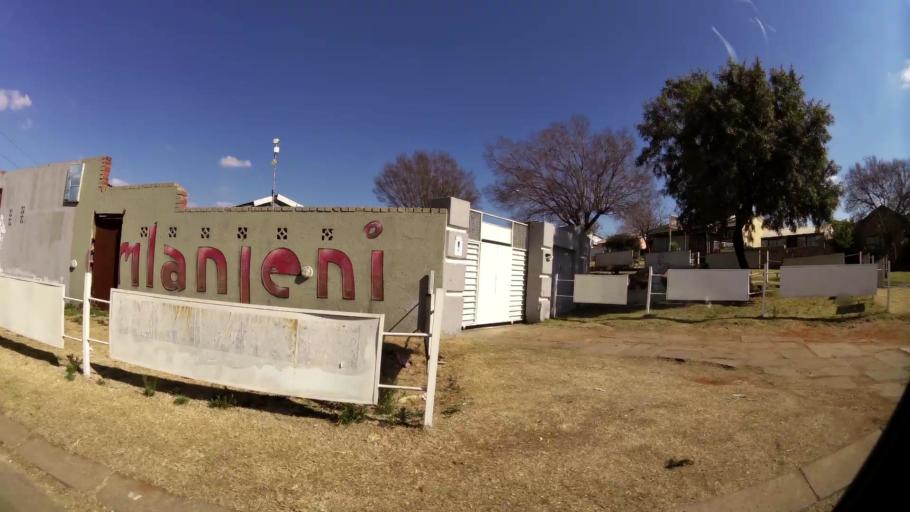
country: ZA
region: Gauteng
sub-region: City of Johannesburg Metropolitan Municipality
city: Soweto
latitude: -26.2427
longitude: 27.9094
